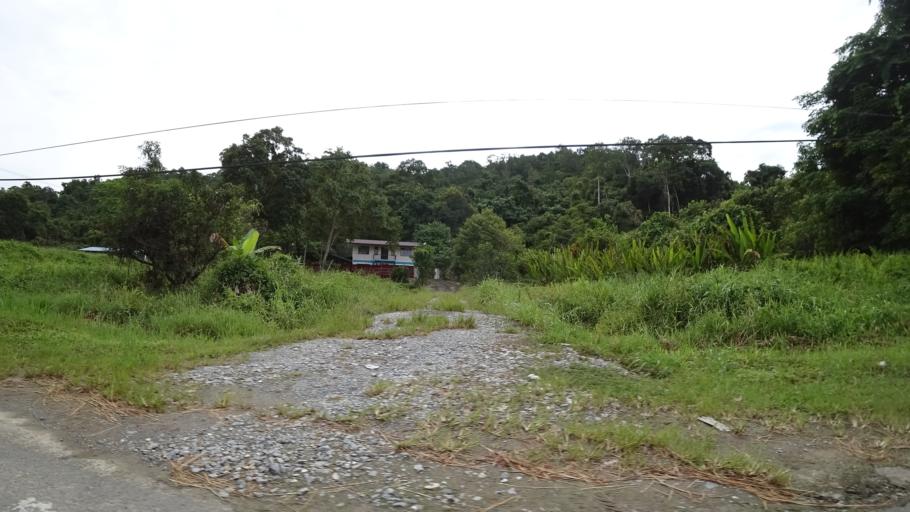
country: MY
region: Sarawak
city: Limbang
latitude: 4.6694
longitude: 114.9857
